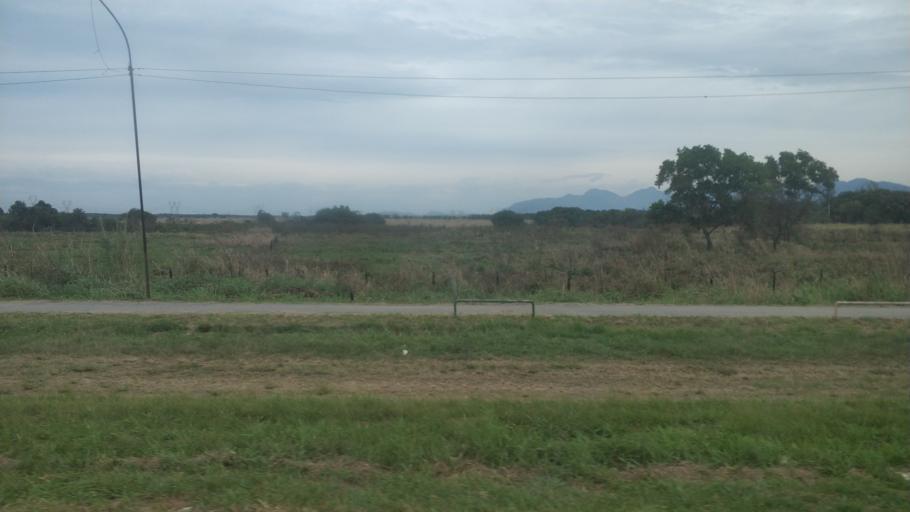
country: BR
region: Rio de Janeiro
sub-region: Seropedica
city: Seropedica
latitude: -22.7787
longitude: -43.6619
